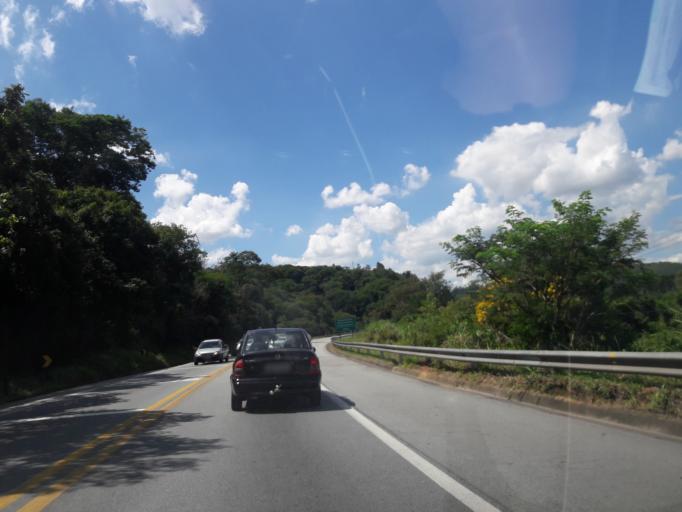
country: BR
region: Sao Paulo
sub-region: Francisco Morato
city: Francisco Morato
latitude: -23.2922
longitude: -46.8044
